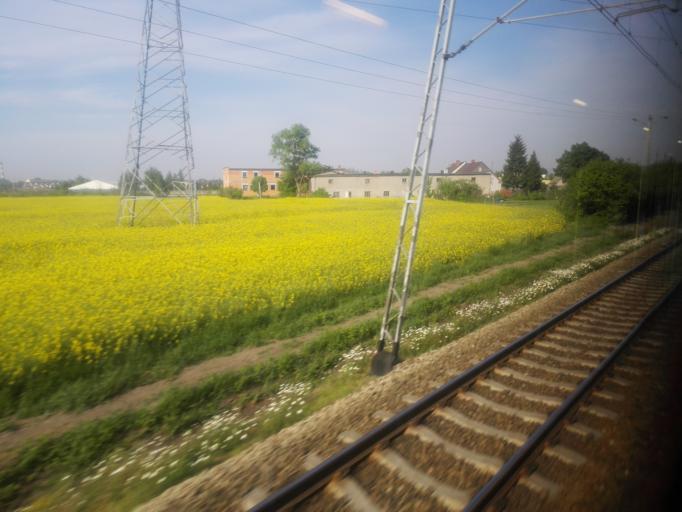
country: PL
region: Greater Poland Voivodeship
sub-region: Powiat wrzesinski
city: Wrzesnia
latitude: 52.3361
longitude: 17.6010
